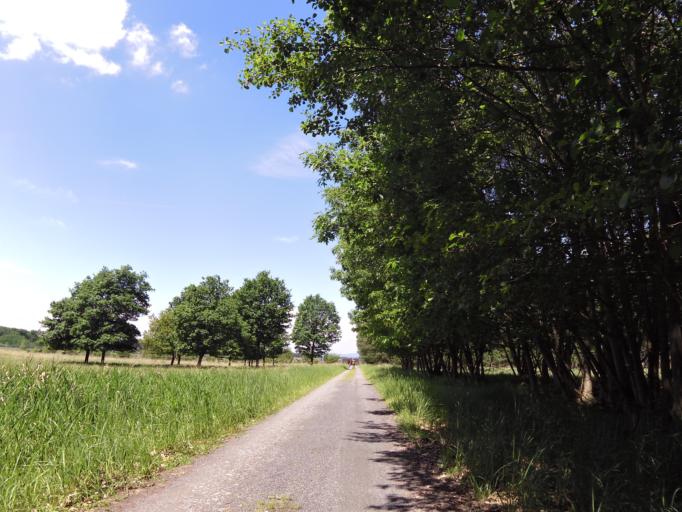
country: DE
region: Hesse
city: Morfelden-Walldorf
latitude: 49.9945
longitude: 8.5293
